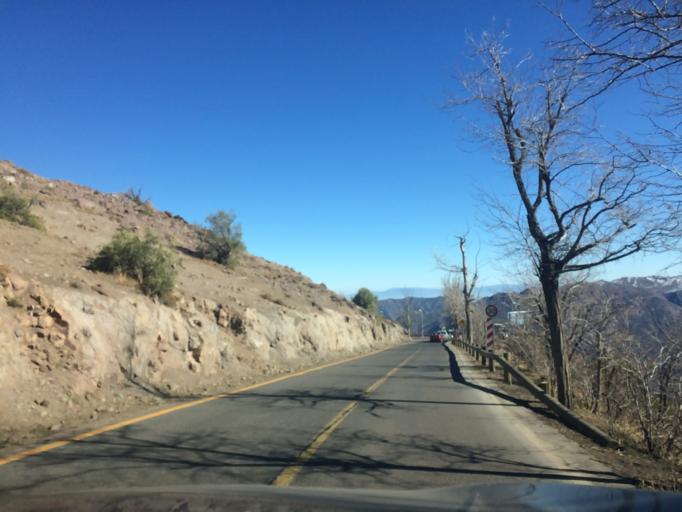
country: CL
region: Santiago Metropolitan
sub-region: Provincia de Santiago
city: Villa Presidente Frei, Nunoa, Santiago, Chile
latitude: -33.3569
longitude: -70.3223
